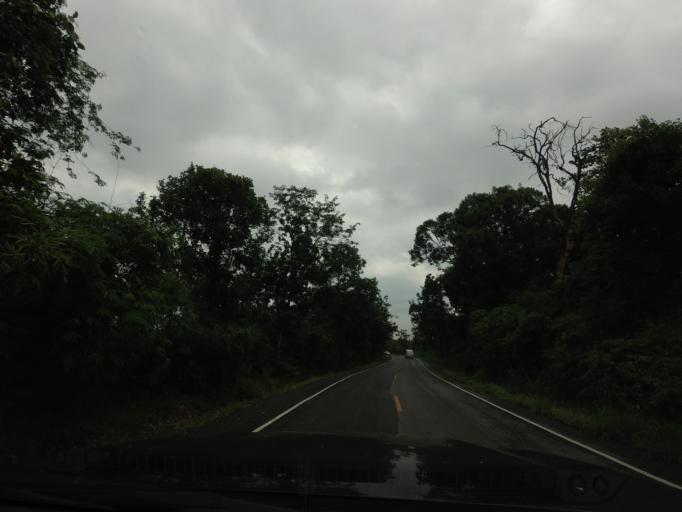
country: TH
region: Nong Khai
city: Sangkhom
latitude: 18.0386
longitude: 102.3292
